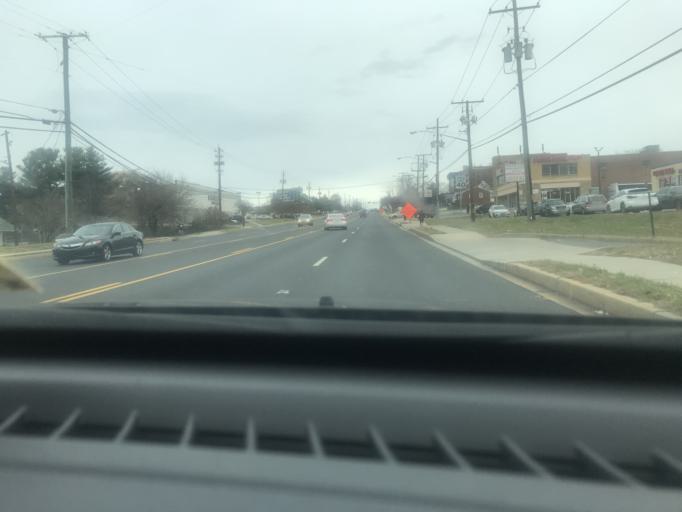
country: US
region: Maryland
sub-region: Prince George's County
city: Oxon Hill
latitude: 38.8036
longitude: -76.9872
